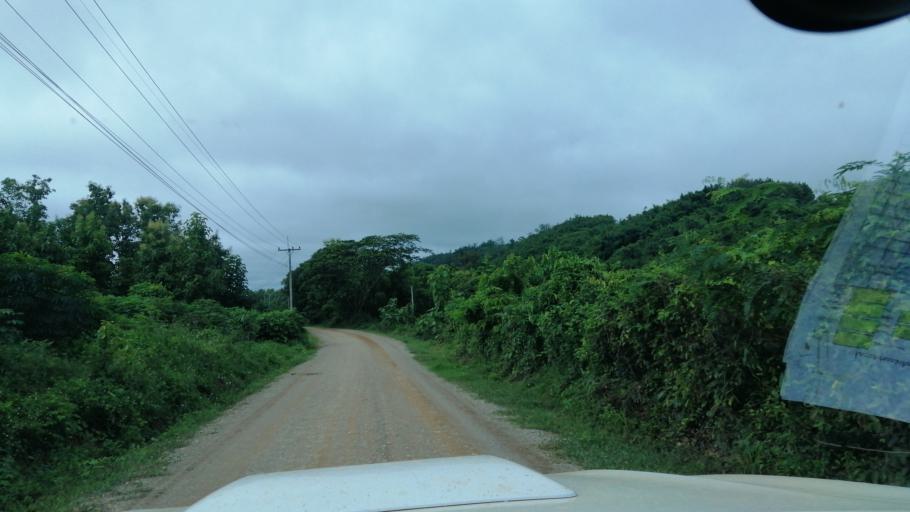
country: LA
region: Xiagnabouli
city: Muang Kenthao
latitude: 17.9718
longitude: 101.4127
